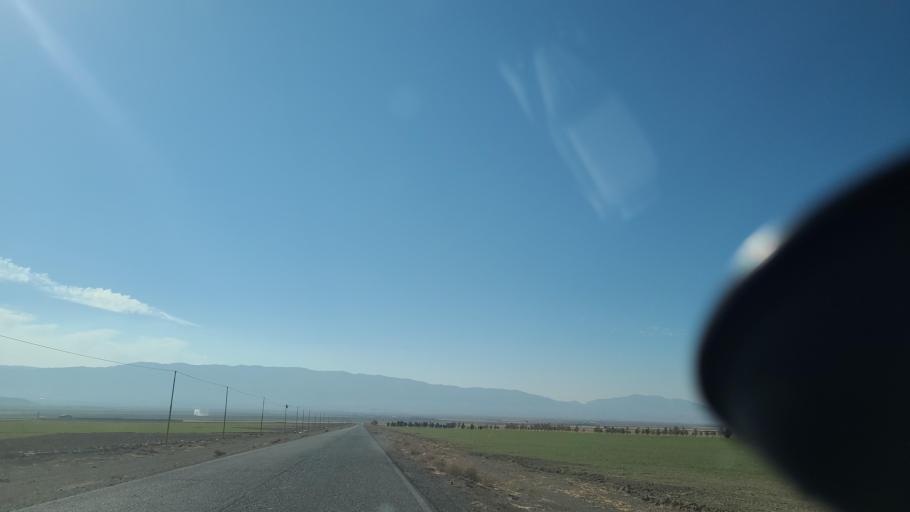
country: IR
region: Razavi Khorasan
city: Dowlatabad
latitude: 35.6077
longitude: 59.4660
